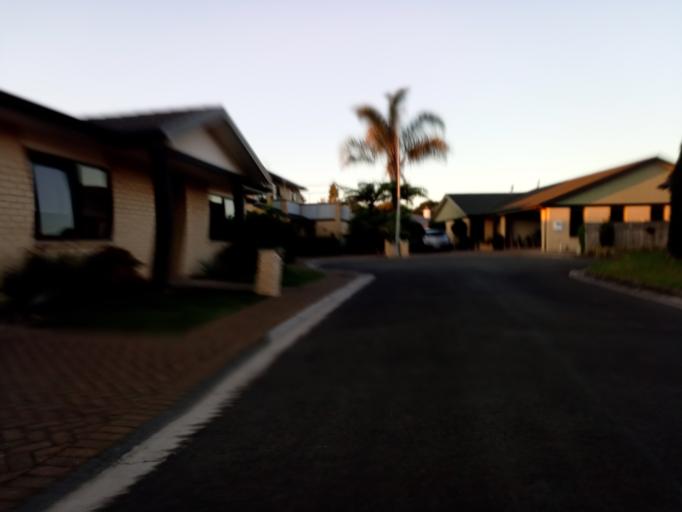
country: NZ
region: Gisborne
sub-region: Gisborne District
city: Gisborne
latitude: -38.6422
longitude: 178.0051
